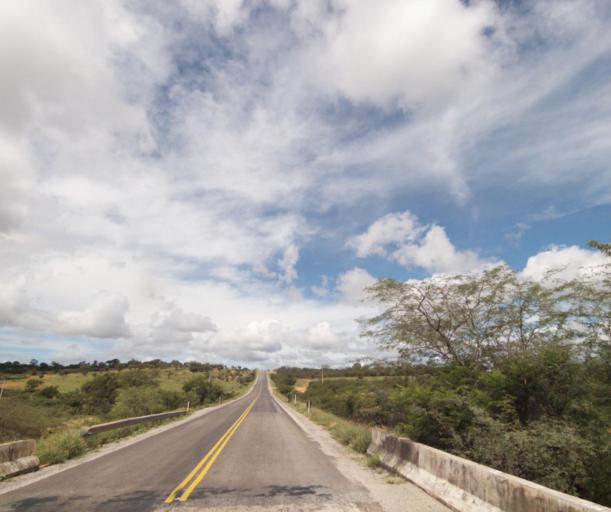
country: BR
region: Bahia
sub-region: Tanhacu
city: Tanhacu
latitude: -14.1564
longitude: -41.2644
